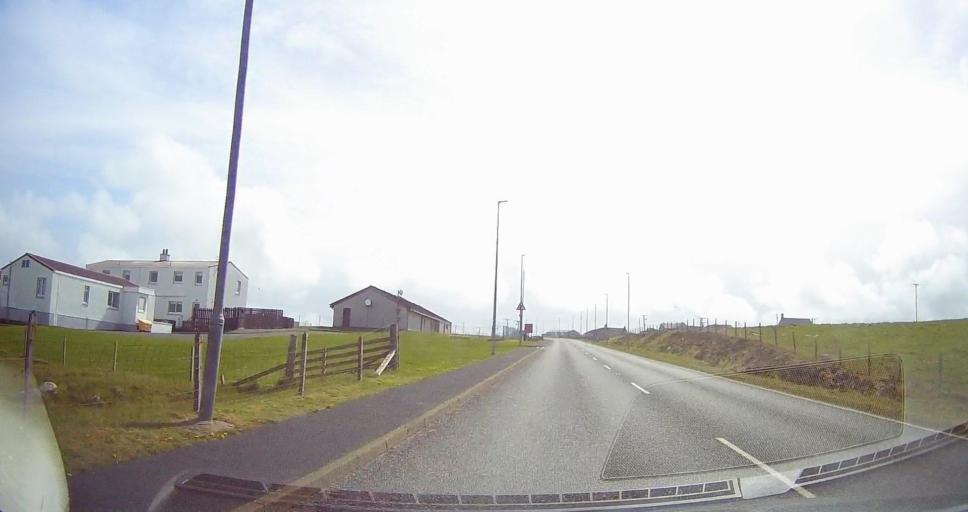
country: GB
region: Scotland
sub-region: Shetland Islands
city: Sandwick
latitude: 59.9228
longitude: -1.2983
